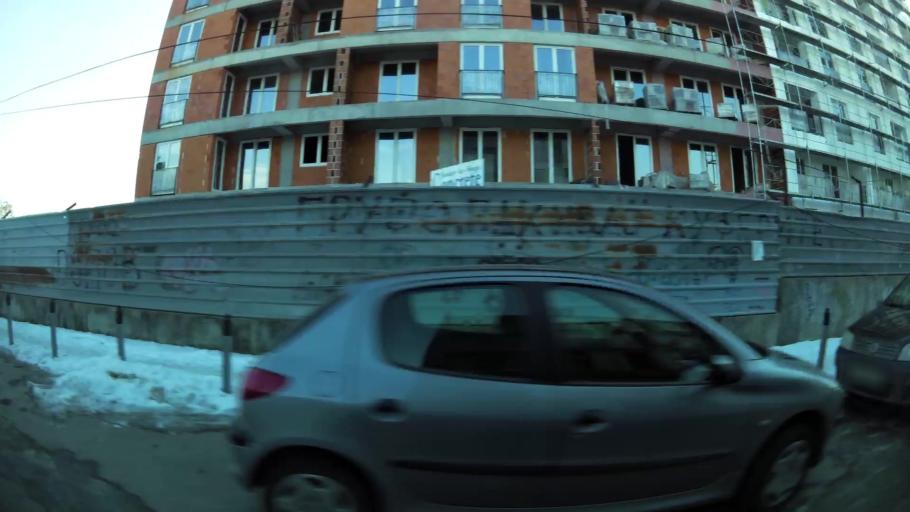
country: MK
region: Karpos
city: Skopje
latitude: 41.9985
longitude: 21.3986
